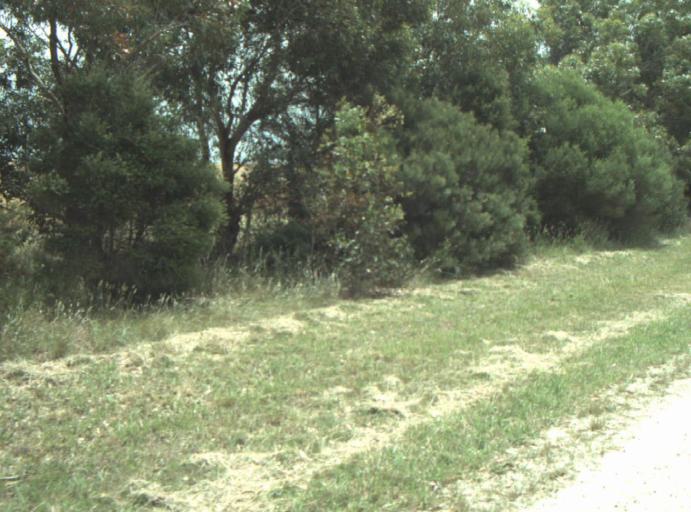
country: AU
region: Victoria
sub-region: Greater Geelong
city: Wandana Heights
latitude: -38.2347
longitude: 144.2976
